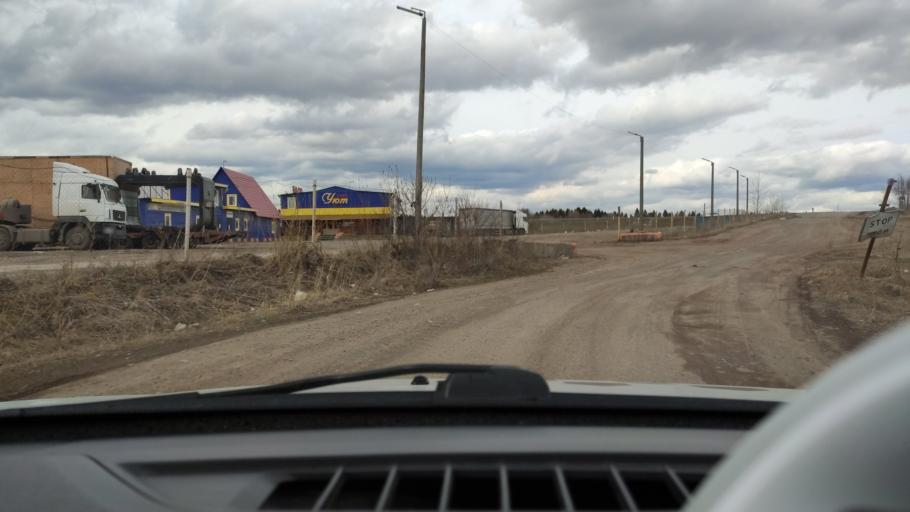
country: RU
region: Perm
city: Froly
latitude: 57.9329
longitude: 56.2368
